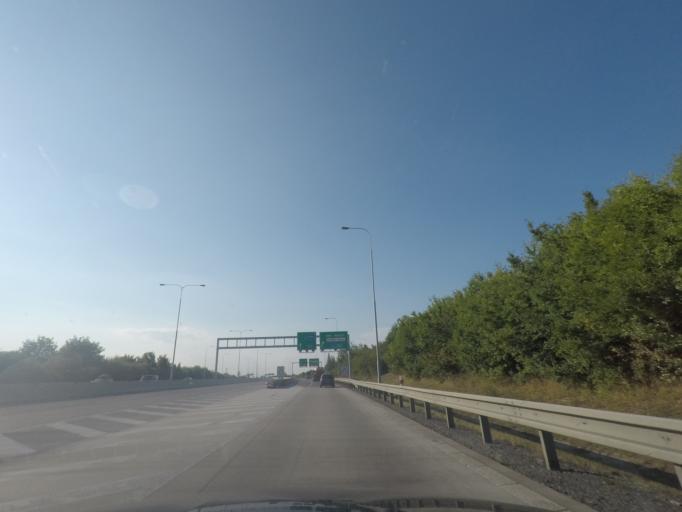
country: CZ
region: Olomoucky
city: Hnevotin
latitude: 49.5639
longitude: 17.2202
